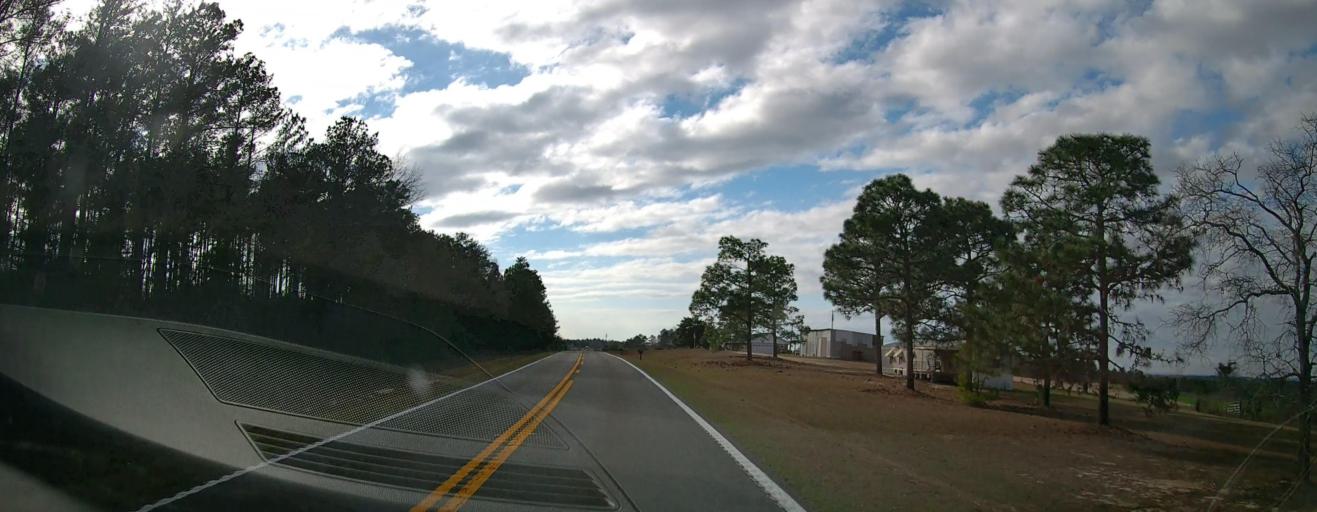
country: US
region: Georgia
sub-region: Marion County
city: Buena Vista
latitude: 32.4442
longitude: -84.5184
